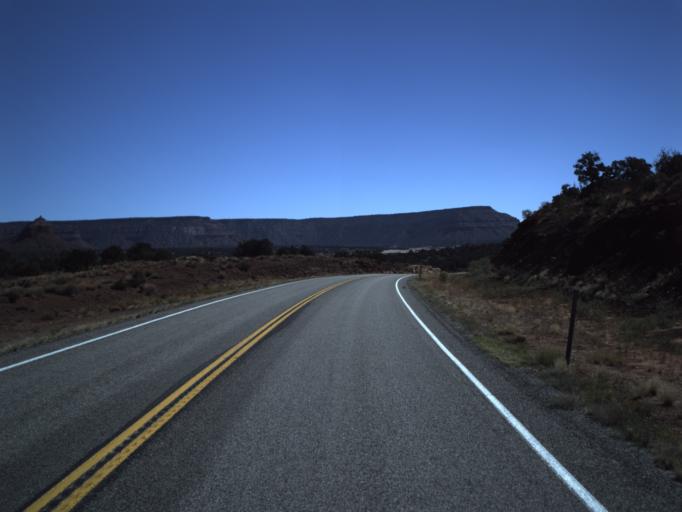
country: US
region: Utah
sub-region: San Juan County
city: Blanding
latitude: 37.6513
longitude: -110.1228
